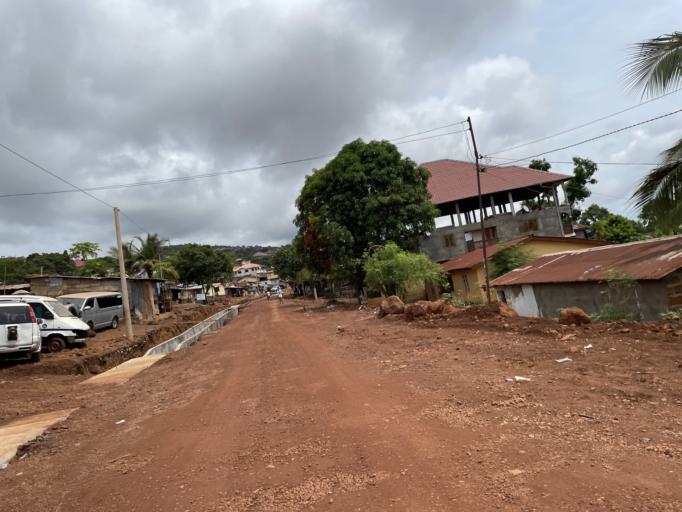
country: SL
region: Western Area
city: Hastings
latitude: 8.4134
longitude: -13.1520
